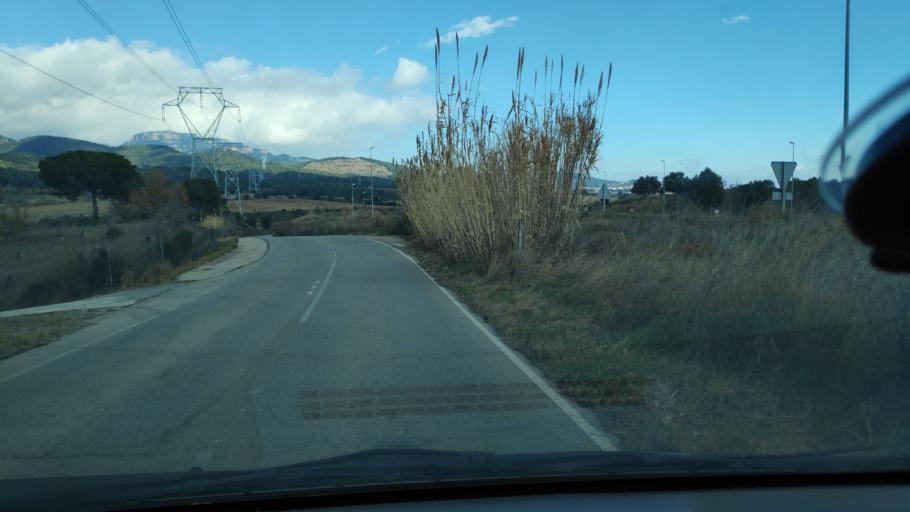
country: ES
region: Catalonia
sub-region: Provincia de Barcelona
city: Terrassa
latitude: 41.5810
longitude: 1.9892
